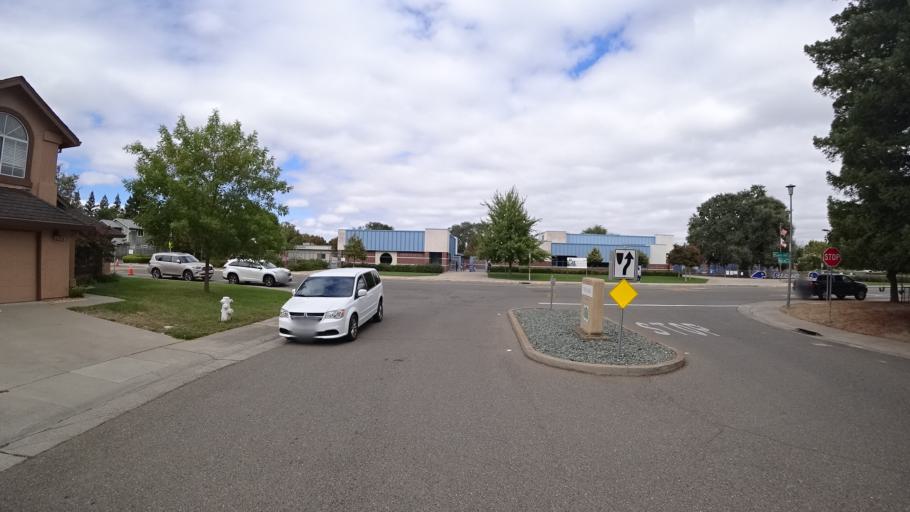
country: US
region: California
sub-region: Sacramento County
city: Laguna
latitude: 38.4178
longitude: -121.4317
